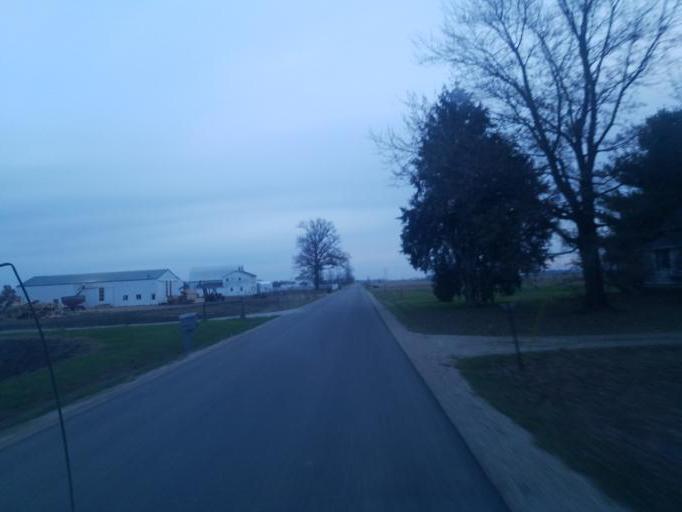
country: US
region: Indiana
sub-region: Adams County
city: Berne
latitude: 40.7374
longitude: -84.9947
